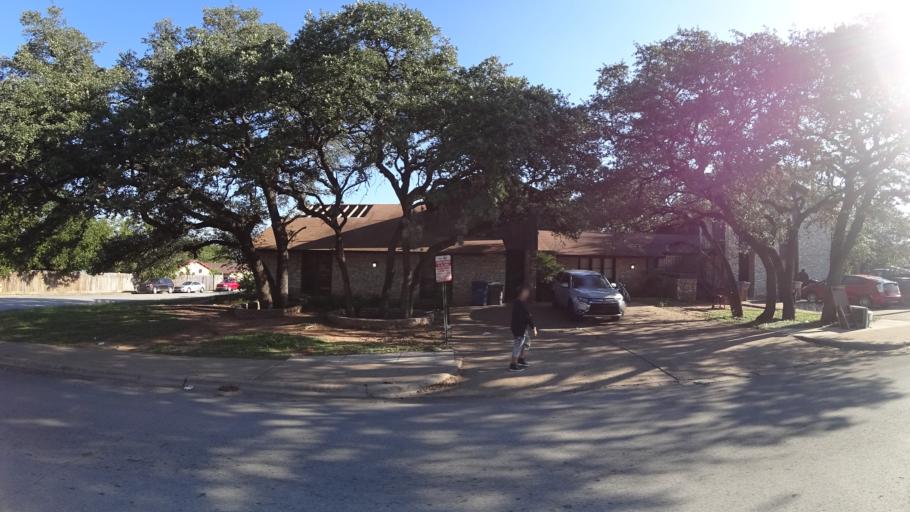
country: US
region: Texas
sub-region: Travis County
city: Austin
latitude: 30.3460
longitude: -97.7000
